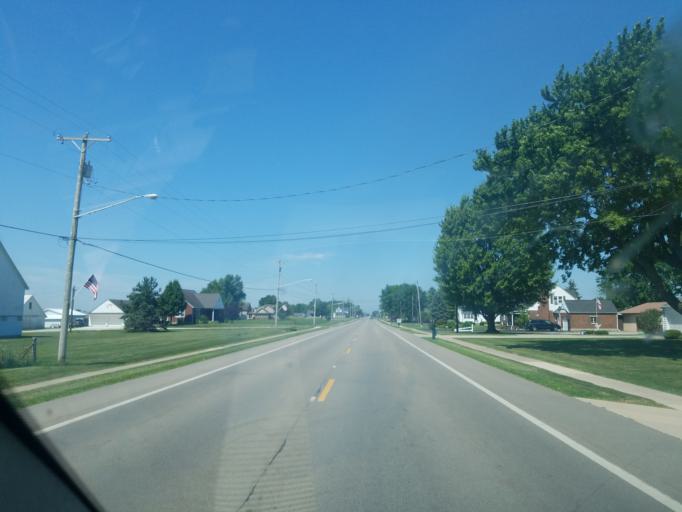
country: US
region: Ohio
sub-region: Auglaize County
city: New Bremen
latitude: 40.4076
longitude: -84.4805
